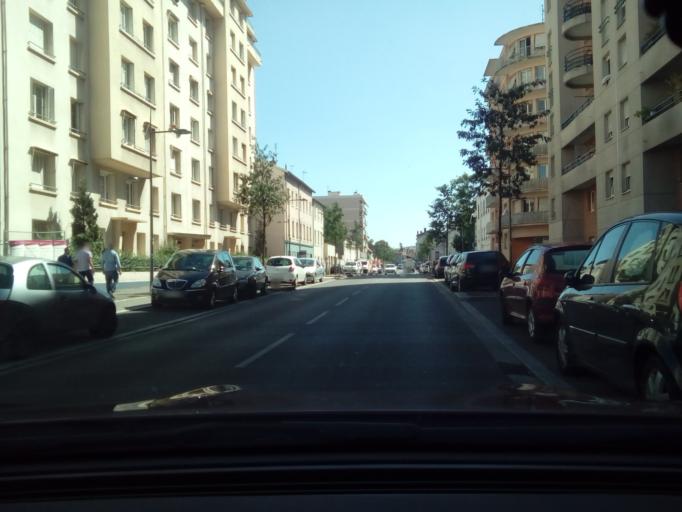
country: FR
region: Rhone-Alpes
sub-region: Departement du Rhone
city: Villeurbanne
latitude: 45.7584
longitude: 4.8766
